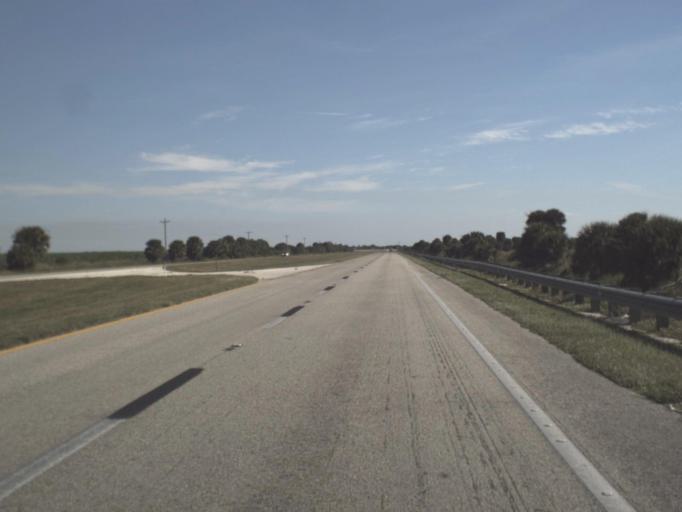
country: US
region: Florida
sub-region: Glades County
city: Moore Haven
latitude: 26.8451
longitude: -81.1996
